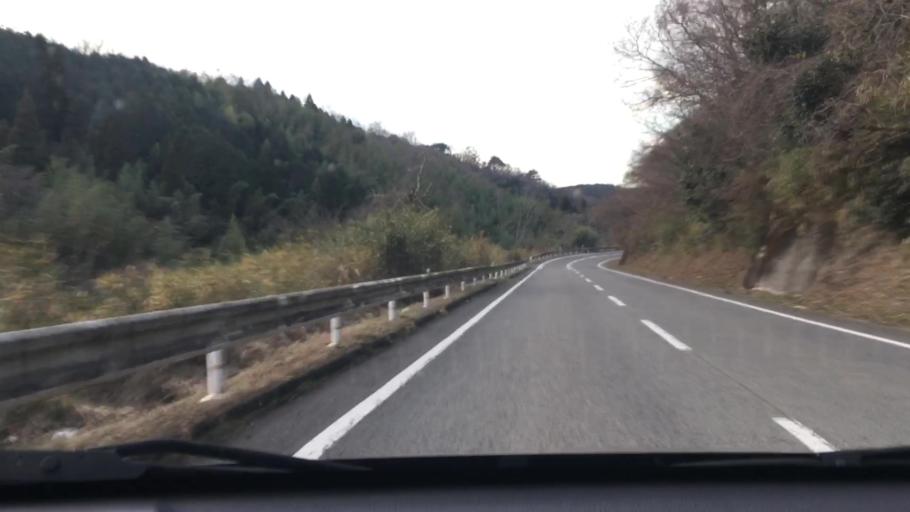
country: JP
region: Oita
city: Hiji
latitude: 33.4095
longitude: 131.4267
